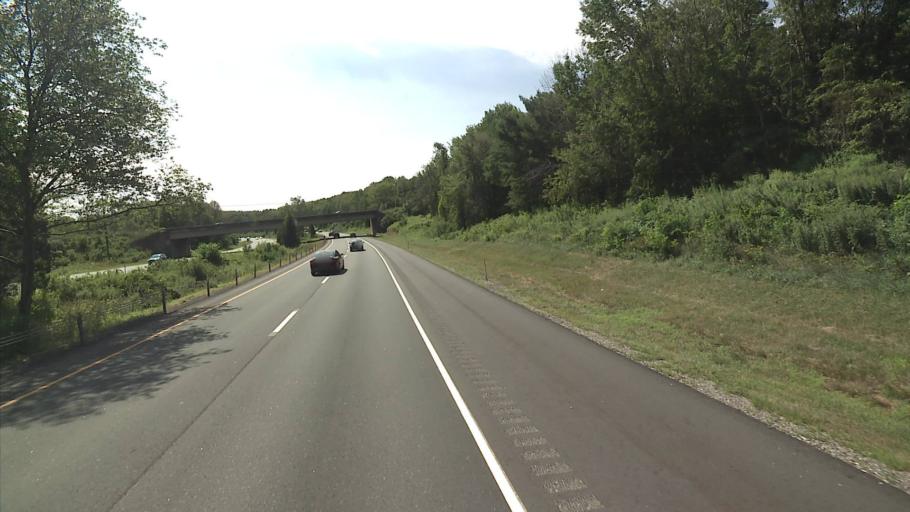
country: US
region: Connecticut
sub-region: Hartford County
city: Terramuggus
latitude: 41.6358
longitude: -72.4595
